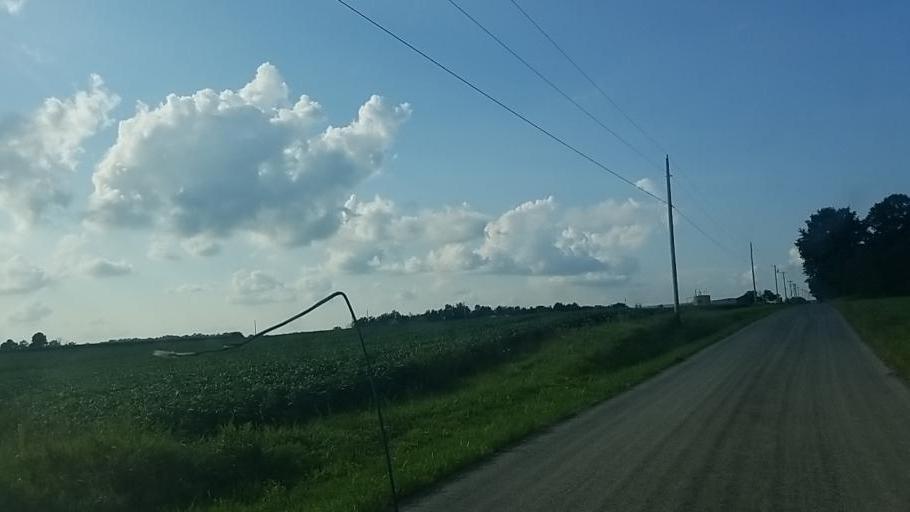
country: US
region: Ohio
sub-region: Wayne County
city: West Salem
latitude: 40.8985
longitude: -82.0376
